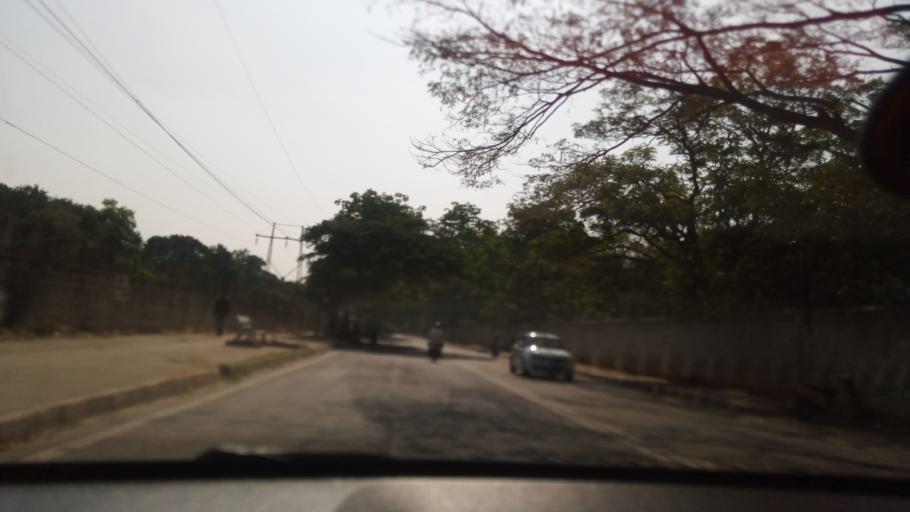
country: IN
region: Karnataka
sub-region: Bangalore Urban
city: Yelahanka
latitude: 13.0502
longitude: 77.5527
